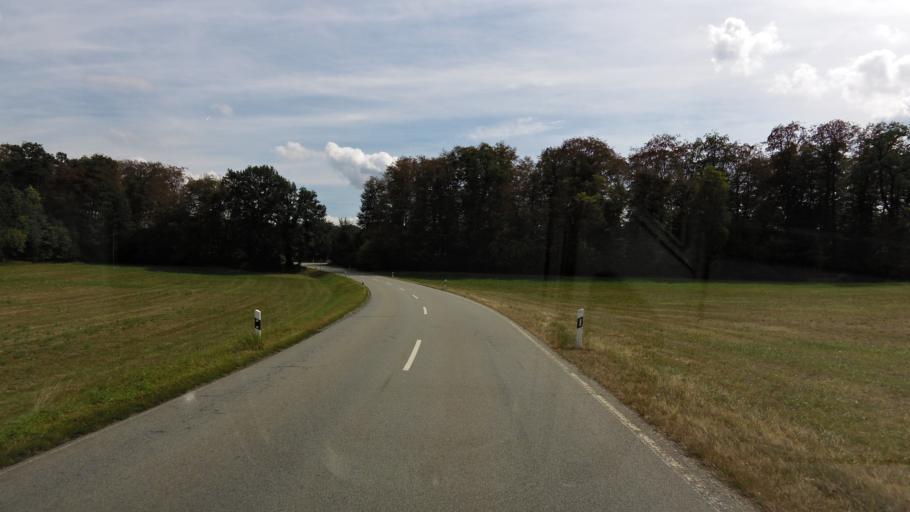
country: DE
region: Bavaria
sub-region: Upper Bavaria
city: Unterneukirchen
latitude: 48.1388
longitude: 12.6311
